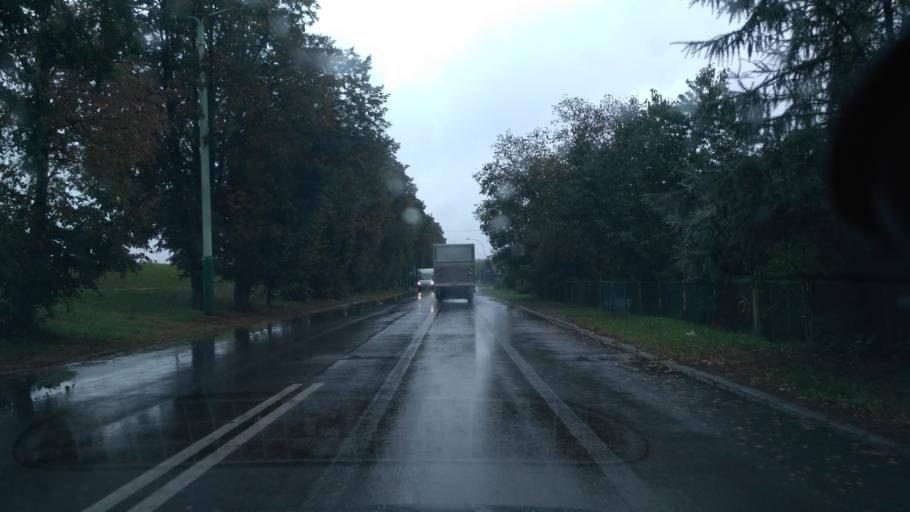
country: PL
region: Subcarpathian Voivodeship
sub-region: Powiat debicki
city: Debica
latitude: 50.0620
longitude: 21.3967
